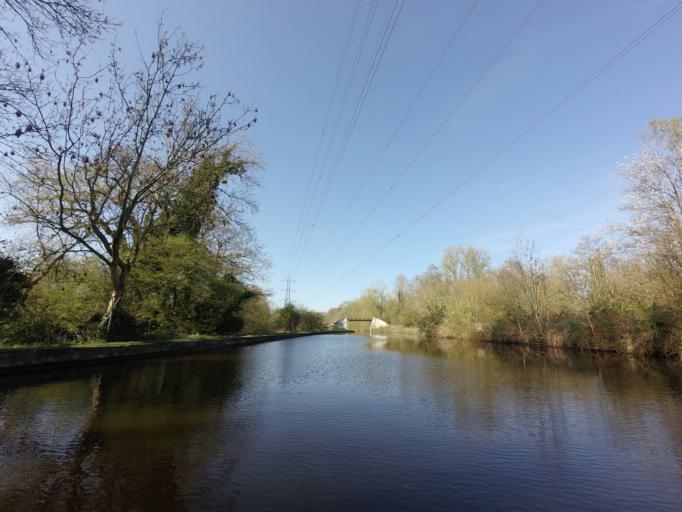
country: GB
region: England
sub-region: Buckinghamshire
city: Denham
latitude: 51.5685
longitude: -0.4819
